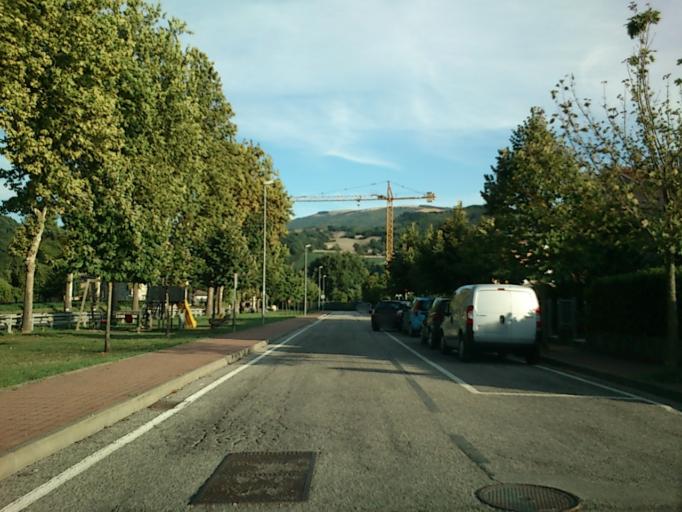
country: IT
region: The Marches
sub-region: Provincia di Pesaro e Urbino
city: Fermignano
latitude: 43.6970
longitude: 12.6662
